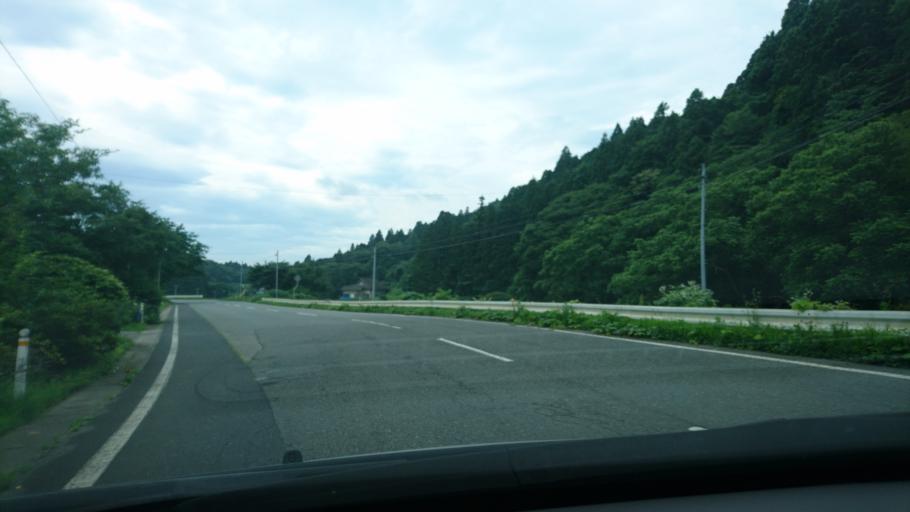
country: JP
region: Iwate
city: Ichinoseki
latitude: 38.8691
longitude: 141.4246
